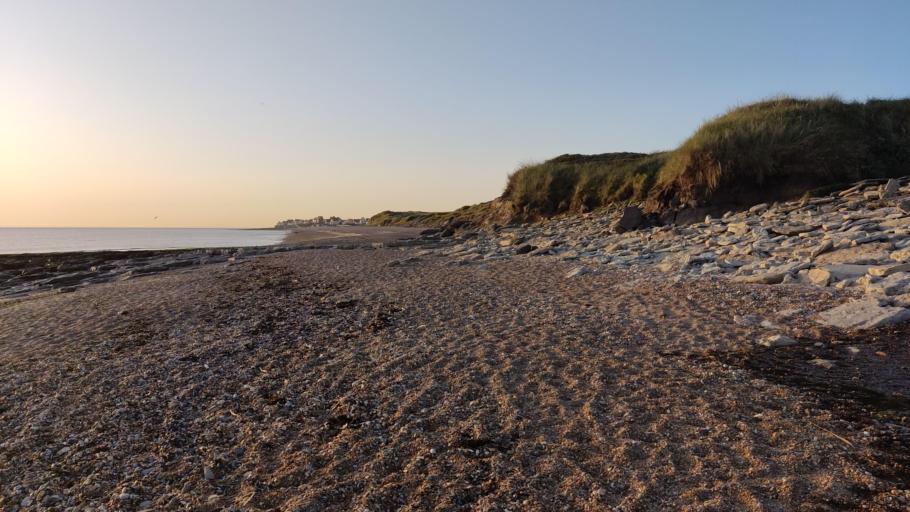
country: FR
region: Nord-Pas-de-Calais
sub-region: Departement du Pas-de-Calais
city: Ambleteuse
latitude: 50.8125
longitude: 1.5971
